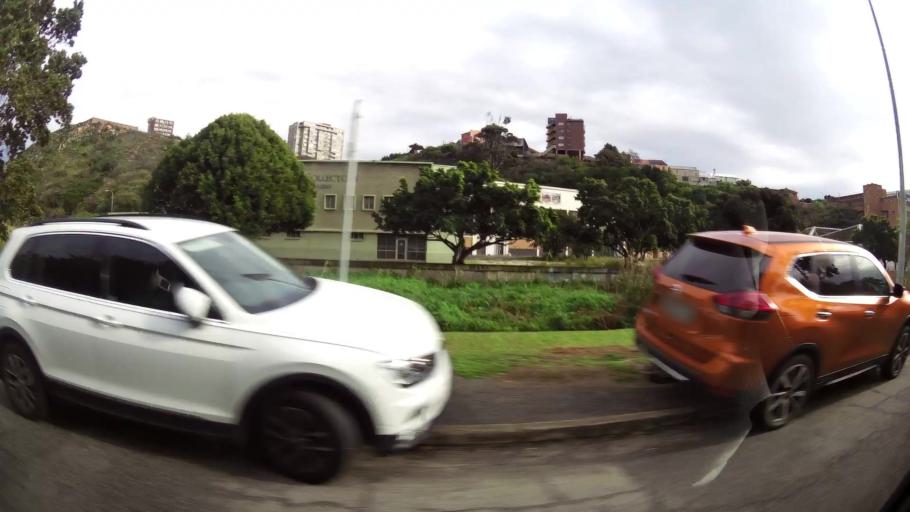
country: ZA
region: Eastern Cape
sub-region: Nelson Mandela Bay Metropolitan Municipality
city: Port Elizabeth
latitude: -33.9662
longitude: 25.6239
